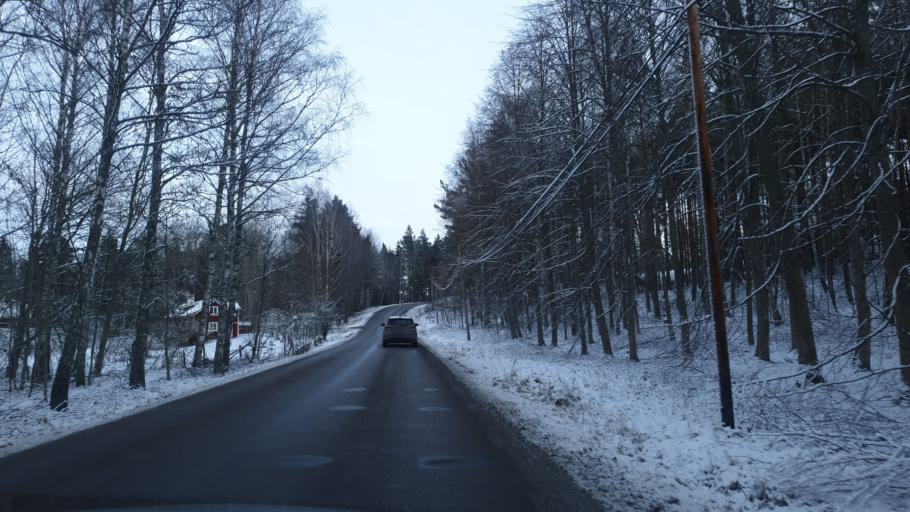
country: SE
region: Uppsala
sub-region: Habo Kommun
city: Balsta
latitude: 59.7061
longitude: 17.5423
